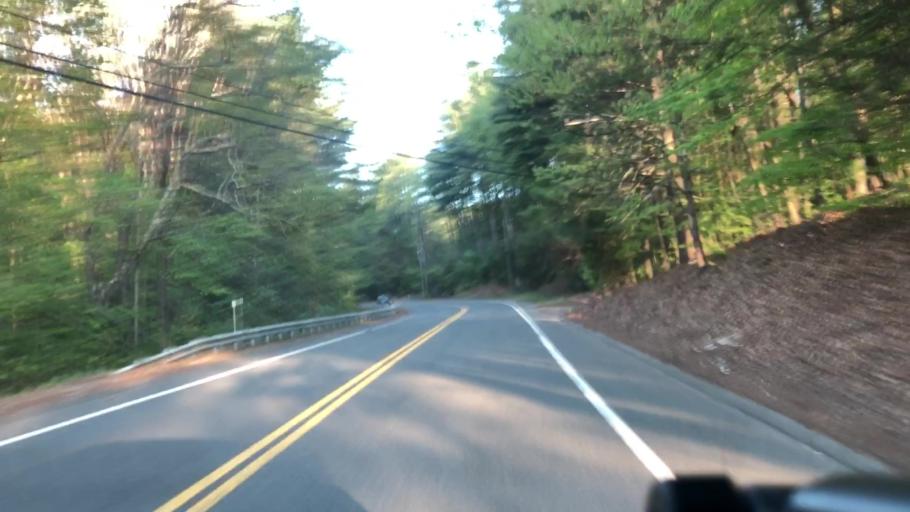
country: US
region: Massachusetts
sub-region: Hampshire County
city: Westhampton
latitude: 42.2833
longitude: -72.7826
